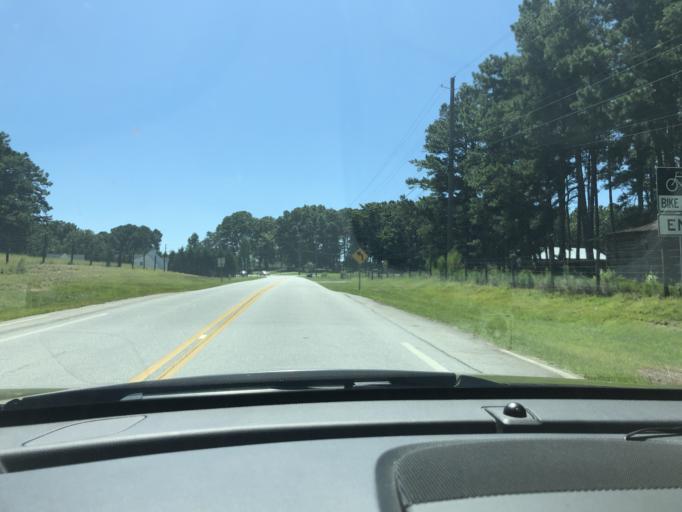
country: US
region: Georgia
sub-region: Gwinnett County
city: Grayson
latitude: 33.9063
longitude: -83.8898
